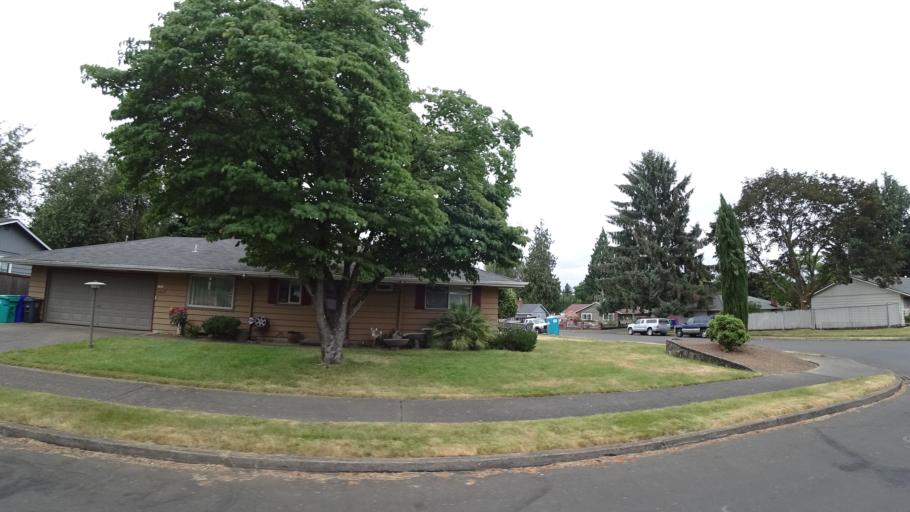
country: US
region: Oregon
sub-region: Multnomah County
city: Portland
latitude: 45.5848
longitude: -122.7046
